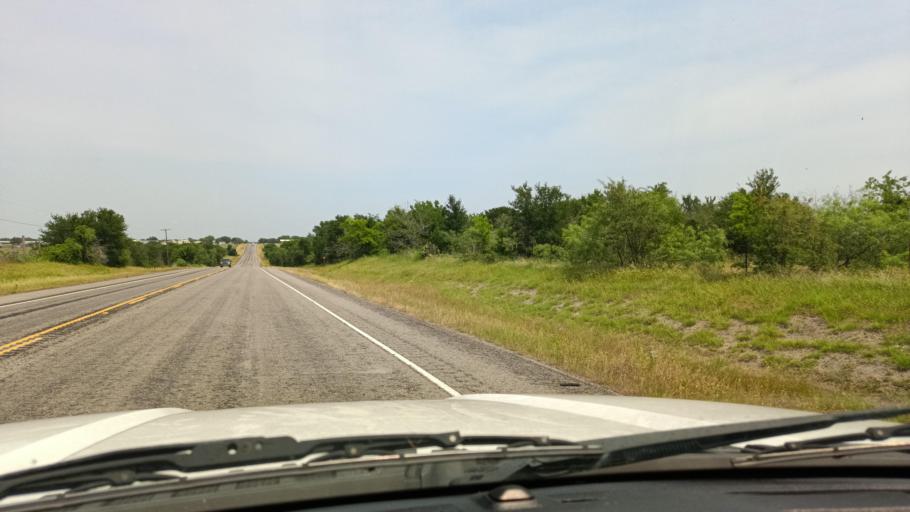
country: US
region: Texas
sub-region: Milam County
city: Cameron
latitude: 30.8554
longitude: -97.1016
